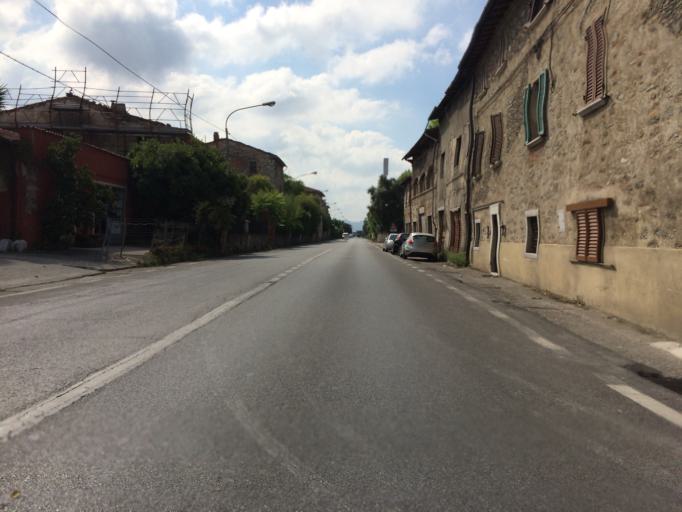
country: IT
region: Tuscany
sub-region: Provincia di Lucca
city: Ripa-Pozzi-Querceta-Ponterosso
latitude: 43.9756
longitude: 10.2016
